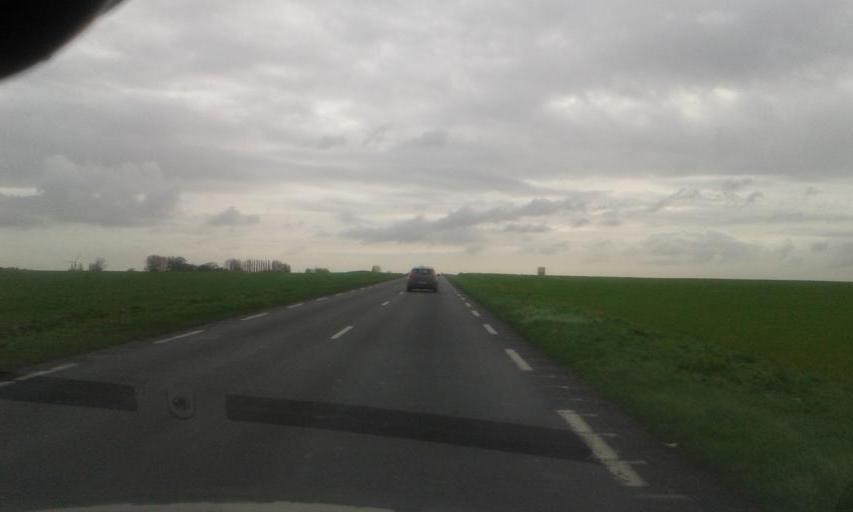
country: FR
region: Haute-Normandie
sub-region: Departement de la Seine-Maritime
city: Montmain
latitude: 49.3860
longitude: 1.2408
